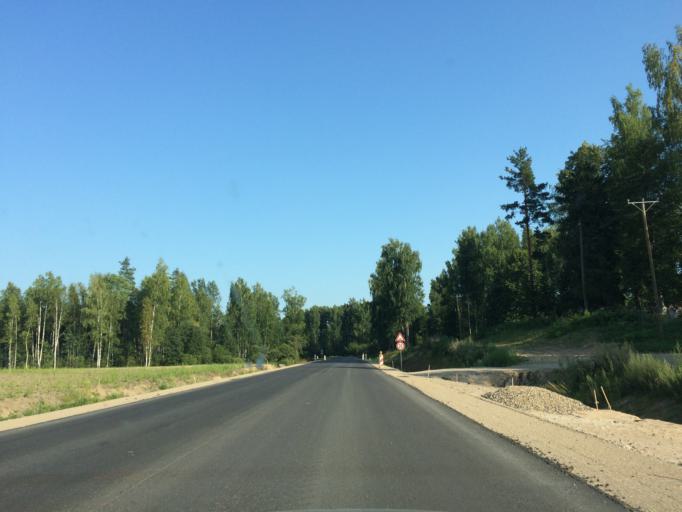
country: LV
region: Rezekne
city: Rezekne
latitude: 56.5148
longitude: 27.4709
